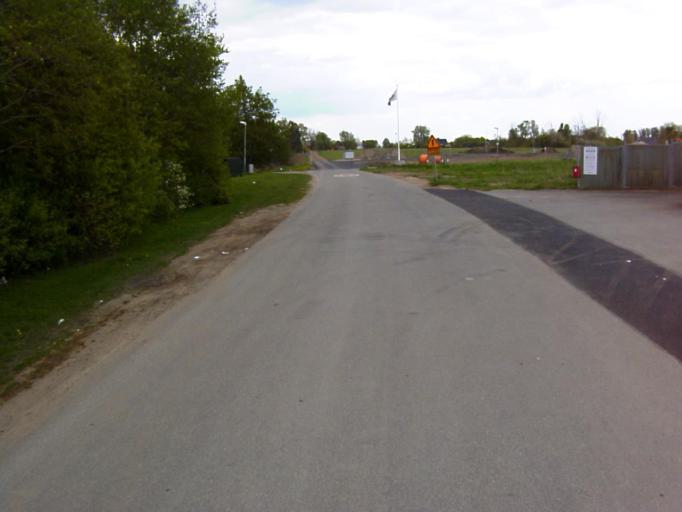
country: SE
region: Skane
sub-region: Kristianstads Kommun
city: Kristianstad
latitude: 56.0163
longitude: 14.2212
